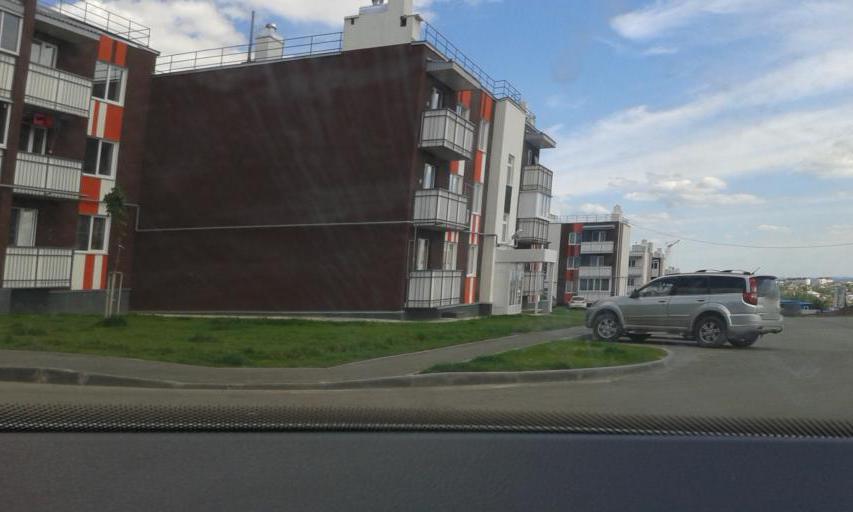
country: RU
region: Volgograd
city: Volgograd
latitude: 48.6626
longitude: 44.4073
